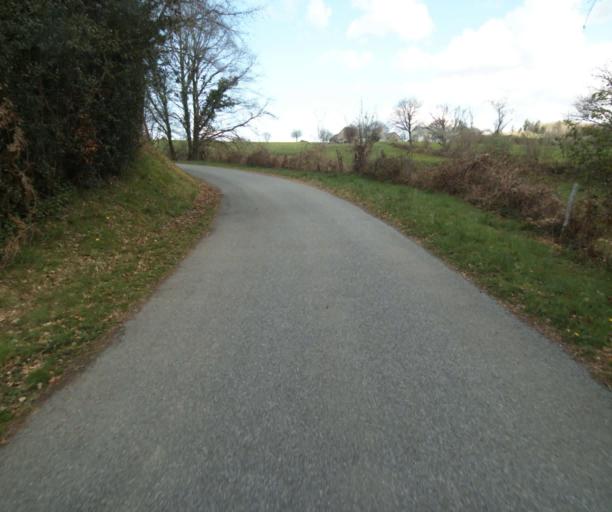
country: FR
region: Limousin
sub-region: Departement de la Correze
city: Laguenne
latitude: 45.2300
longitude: 1.8844
